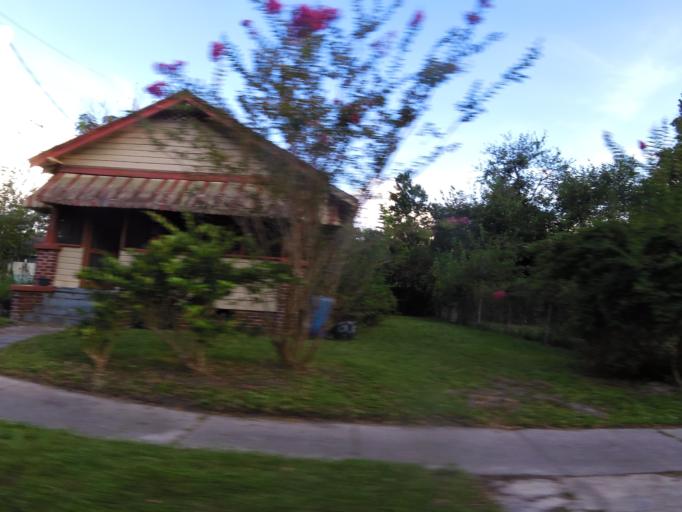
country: US
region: Florida
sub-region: Duval County
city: Jacksonville
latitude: 30.3372
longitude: -81.6949
